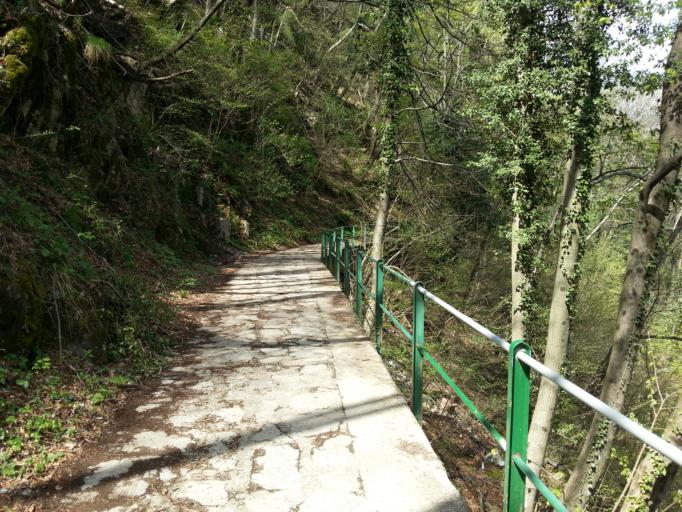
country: IT
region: Lombardy
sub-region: Provincia di Como
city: Torno
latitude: 45.8458
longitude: 9.1274
